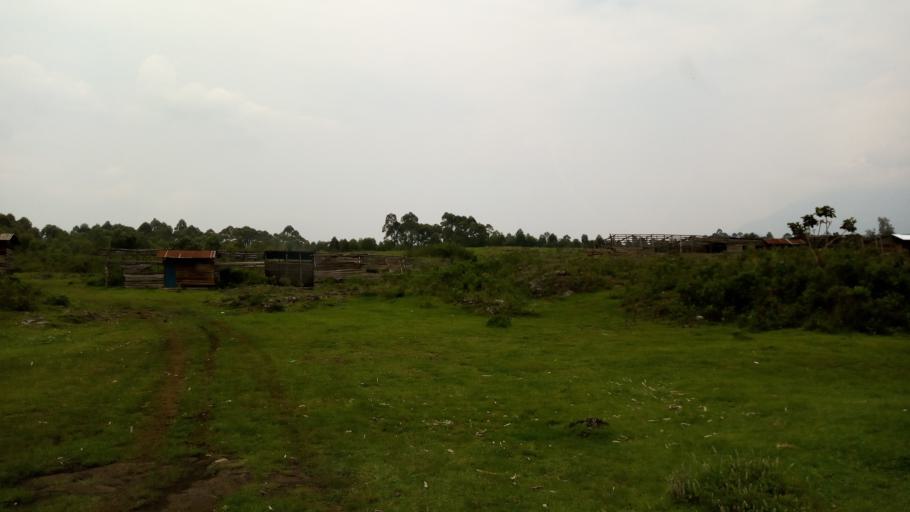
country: UG
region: Western Region
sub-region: Kisoro District
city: Kisoro
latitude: -1.2650
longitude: 29.6015
